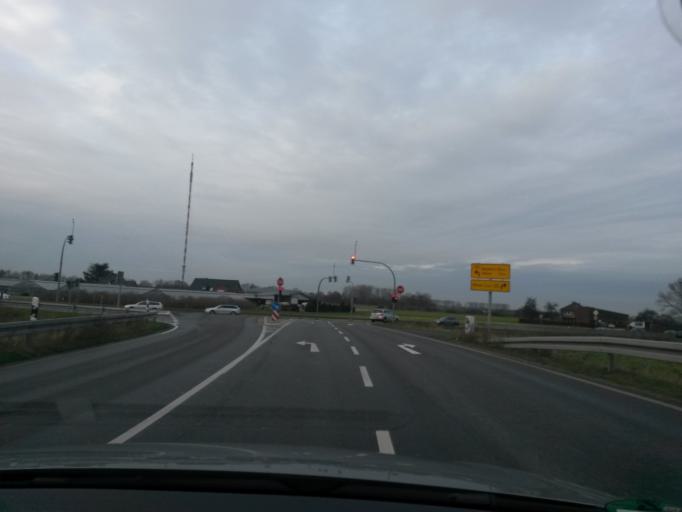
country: DE
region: North Rhine-Westphalia
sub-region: Regierungsbezirk Dusseldorf
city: Wesel
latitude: 51.6392
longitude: 6.5882
